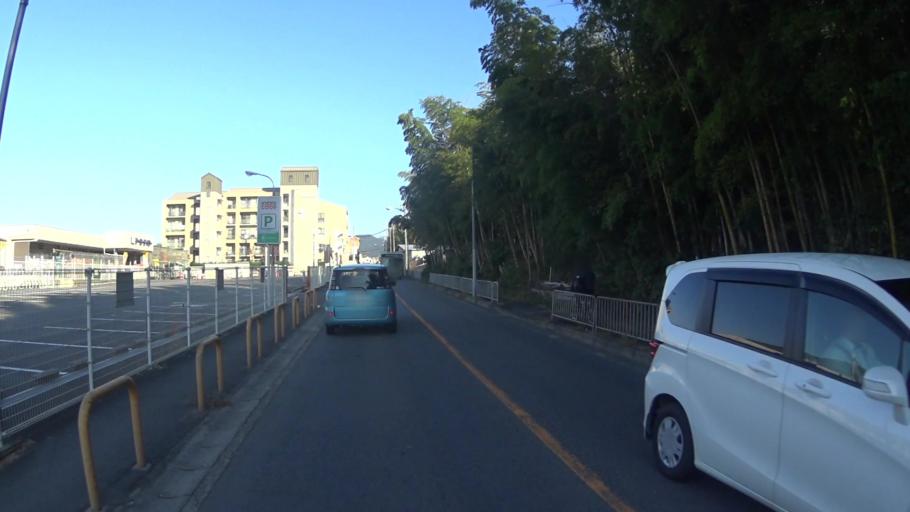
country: JP
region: Kyoto
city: Muko
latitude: 34.9655
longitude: 135.6805
